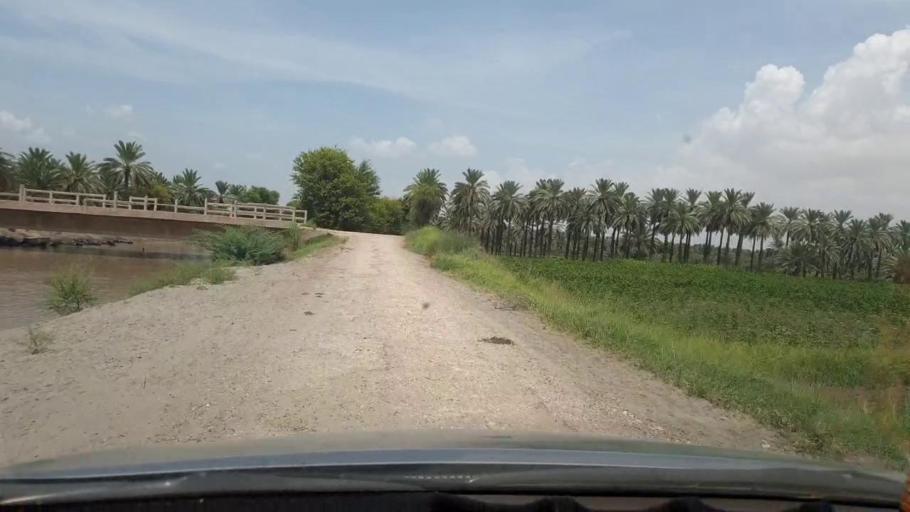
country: PK
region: Sindh
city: Khairpur
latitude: 27.4589
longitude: 68.8020
